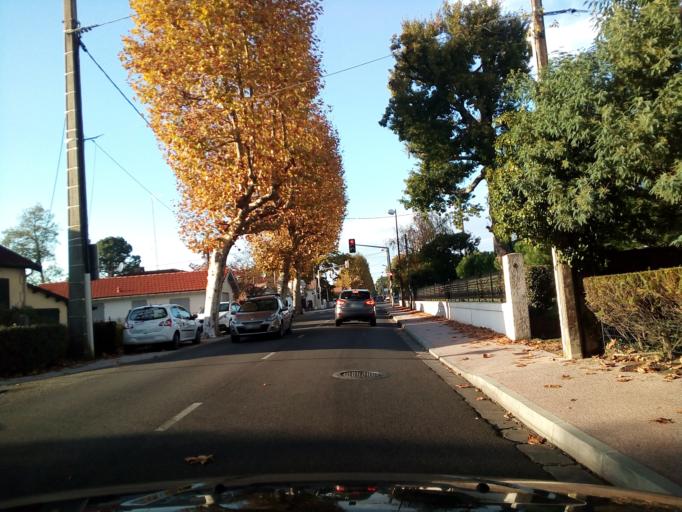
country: FR
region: Aquitaine
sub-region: Departement de la Gironde
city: Andernos-les-Bains
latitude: 44.7441
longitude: -1.1021
